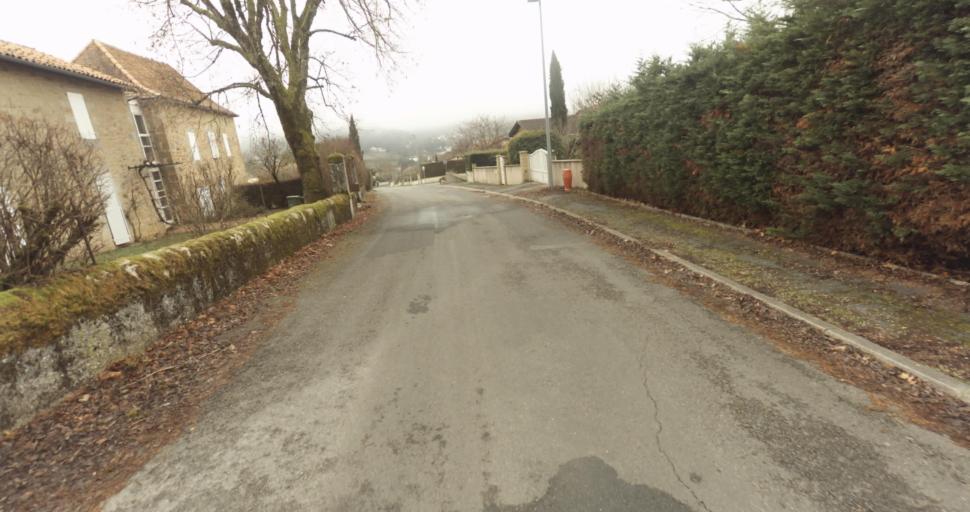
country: FR
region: Midi-Pyrenees
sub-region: Departement du Lot
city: Figeac
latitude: 44.6144
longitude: 2.0423
